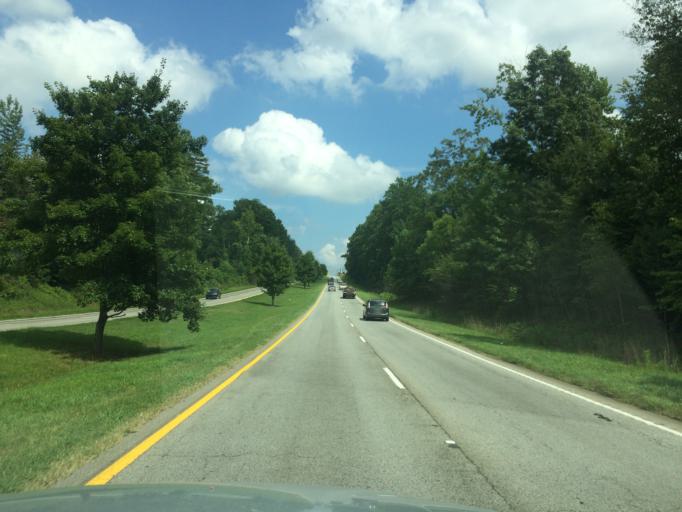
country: US
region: South Carolina
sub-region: Spartanburg County
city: Fairforest
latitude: 34.9394
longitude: -82.0420
